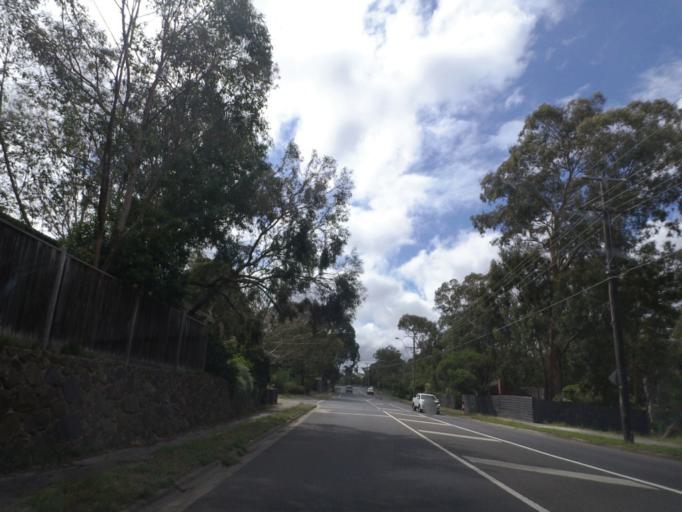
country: AU
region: Victoria
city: Saint Helena
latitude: -37.7076
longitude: 145.1315
